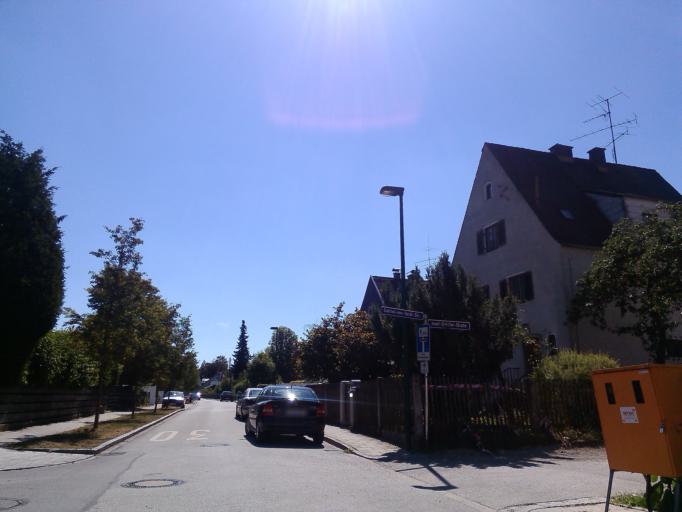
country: DE
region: Bavaria
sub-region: Upper Bavaria
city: Grafelfing
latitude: 48.1323
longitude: 11.4257
